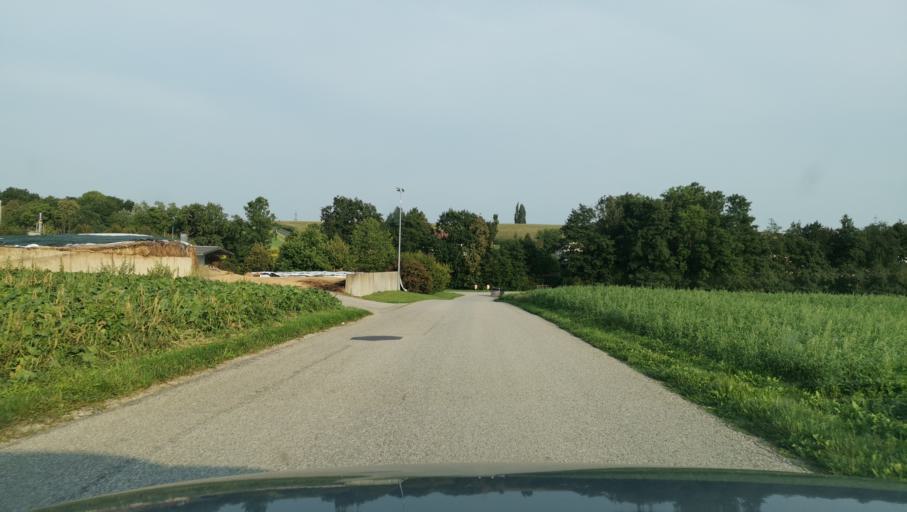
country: AT
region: Upper Austria
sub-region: Politischer Bezirk Grieskirchen
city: Grieskirchen
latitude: 48.2889
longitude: 13.8084
